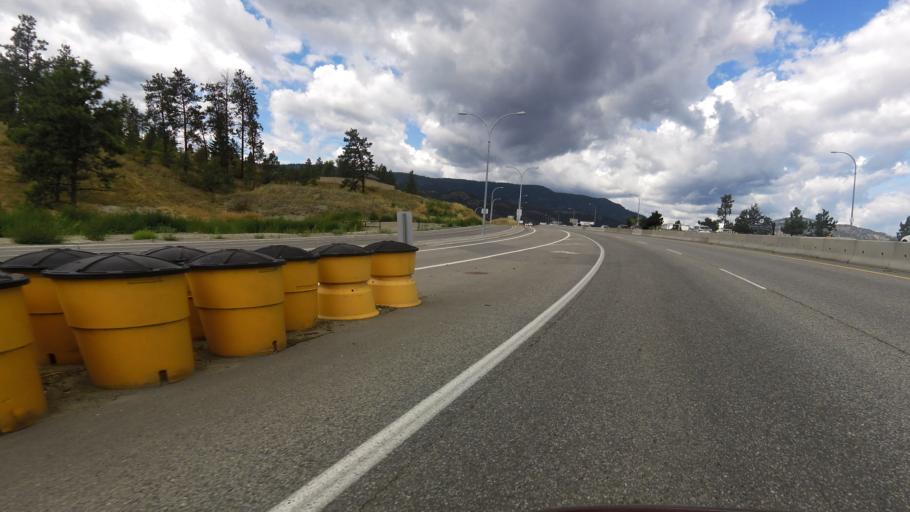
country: CA
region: British Columbia
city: Kelowna
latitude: 49.8817
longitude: -119.5243
